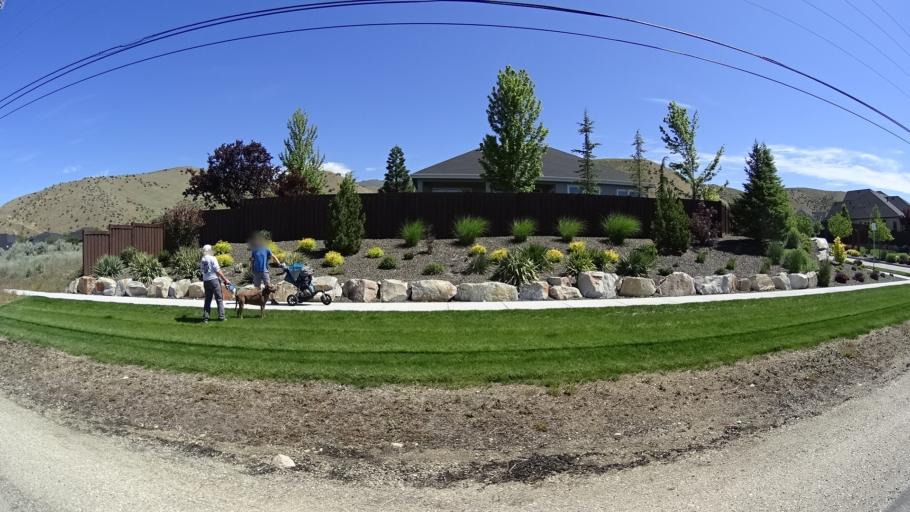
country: US
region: Idaho
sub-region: Ada County
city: Boise
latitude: 43.5610
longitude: -116.1038
